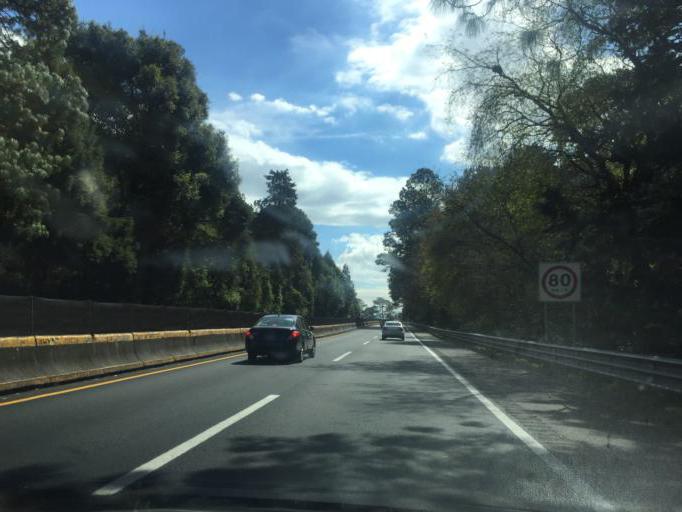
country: MX
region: Morelos
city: Tres Marias
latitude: 19.0320
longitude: -99.2231
